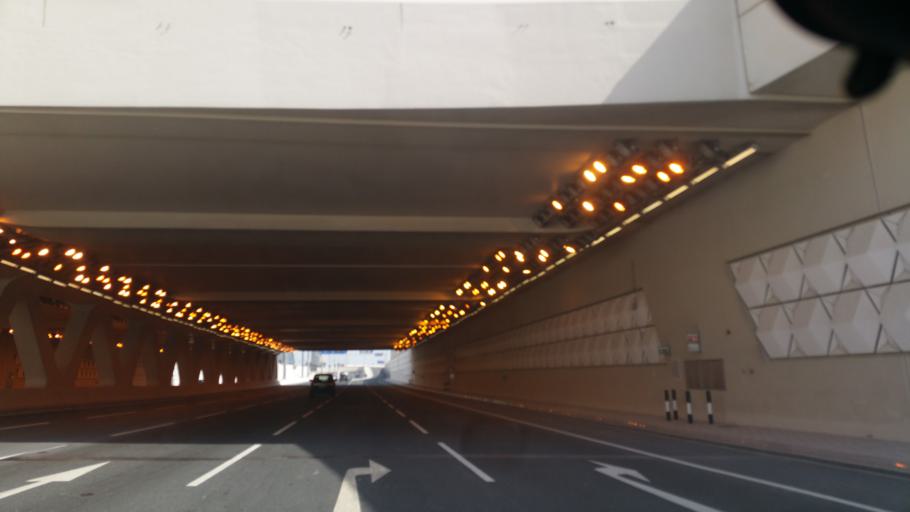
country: QA
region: Baladiyat Umm Salal
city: Umm Salal Muhammad
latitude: 25.3942
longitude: 51.5165
